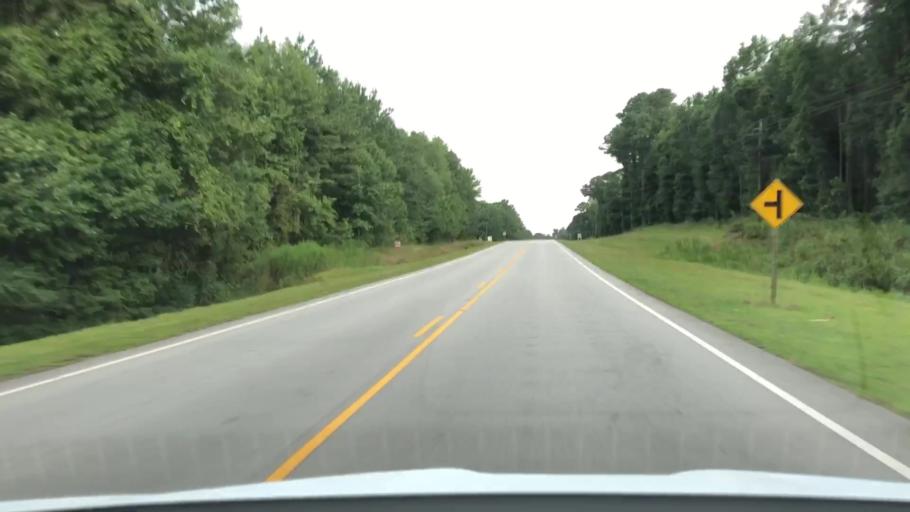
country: US
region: North Carolina
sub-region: Jones County
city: Trenton
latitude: 35.0101
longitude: -77.2875
